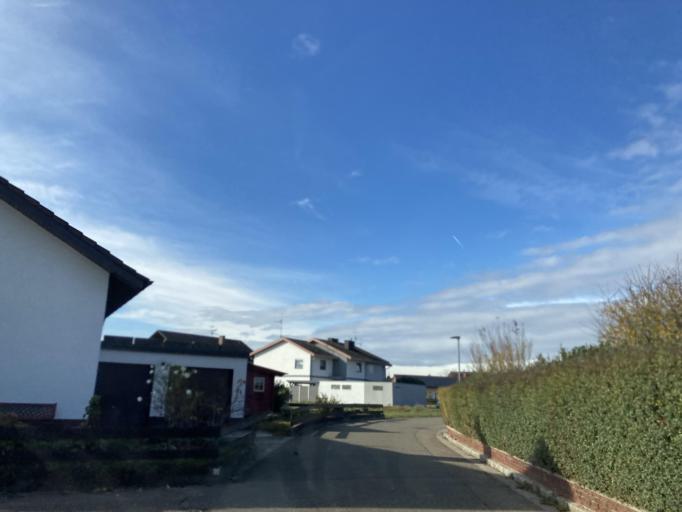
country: DE
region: Baden-Wuerttemberg
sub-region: Freiburg Region
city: Neuenburg am Rhein
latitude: 47.8219
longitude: 7.5655
